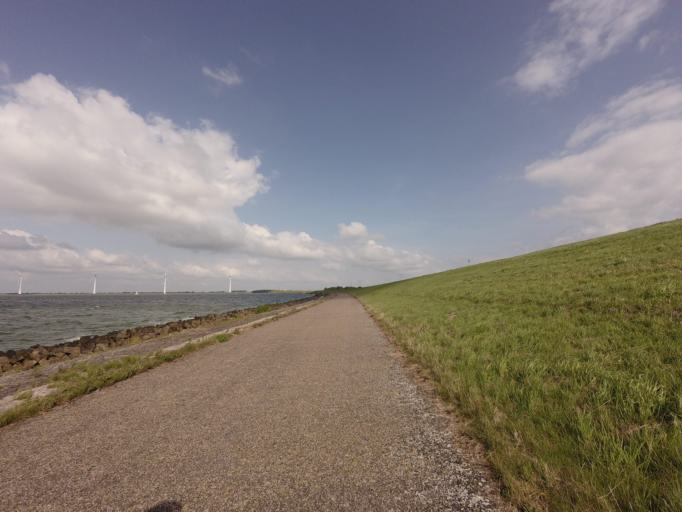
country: NL
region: Flevoland
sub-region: Gemeente Urk
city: Urk
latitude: 52.6046
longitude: 5.6249
